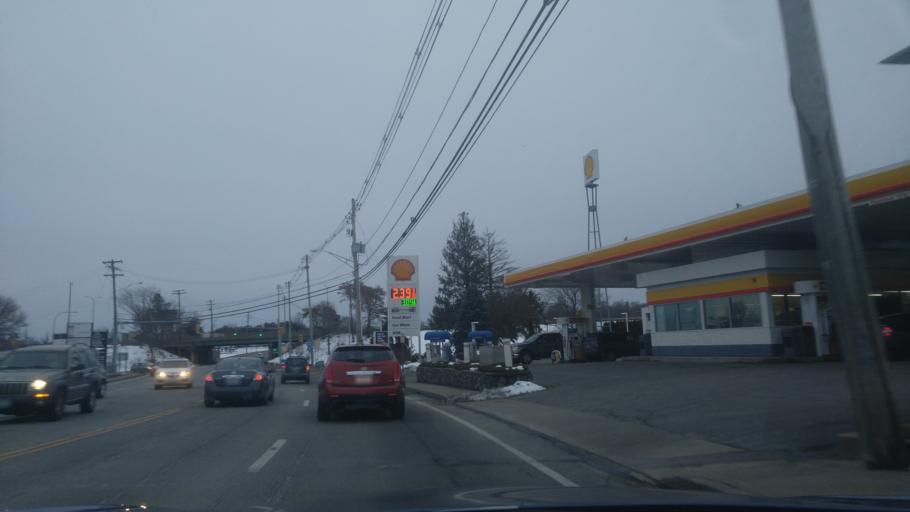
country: US
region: Rhode Island
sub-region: Providence County
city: Cranston
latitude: 41.7517
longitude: -71.4518
